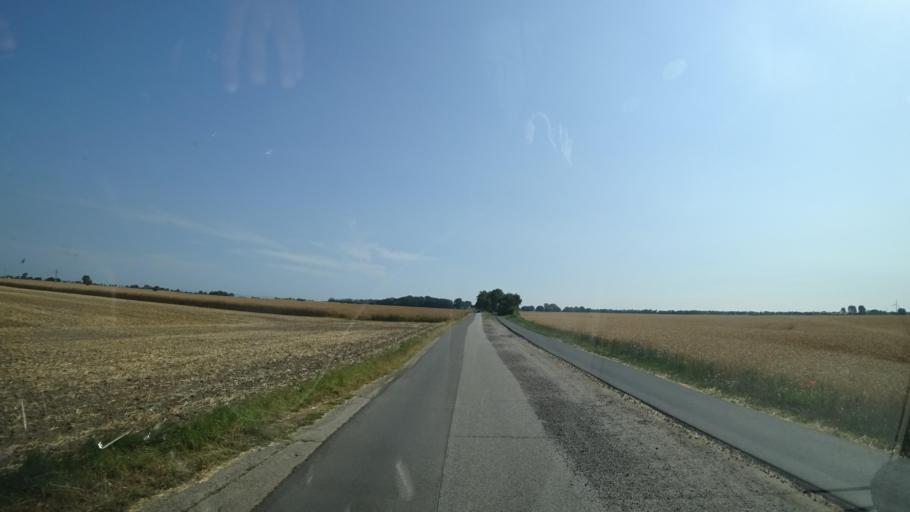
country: DE
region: Mecklenburg-Vorpommern
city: Kemnitz
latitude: 54.1145
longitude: 13.5341
